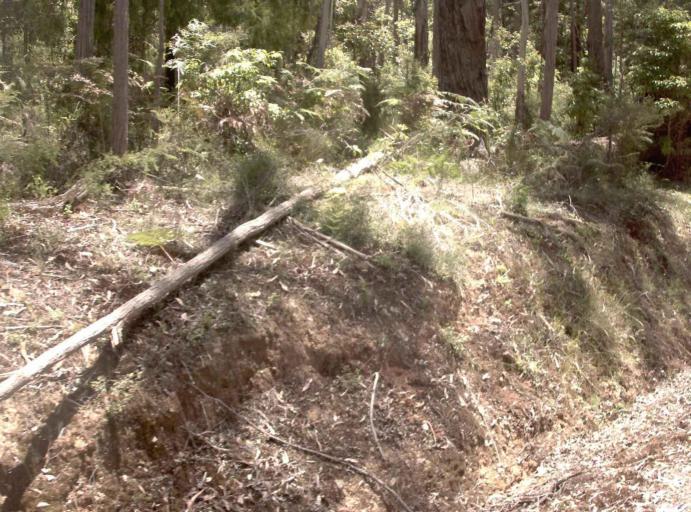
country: AU
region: New South Wales
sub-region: Bombala
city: Bombala
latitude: -37.4885
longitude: 148.9279
